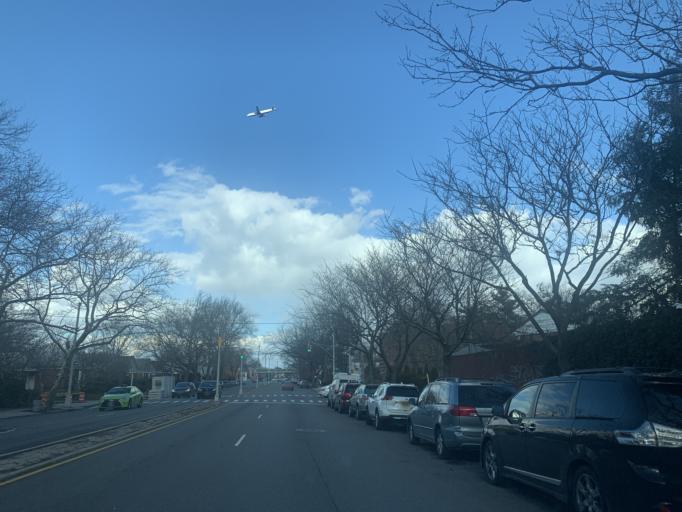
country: US
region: New York
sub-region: Queens County
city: Jamaica
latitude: 40.7358
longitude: -73.7931
